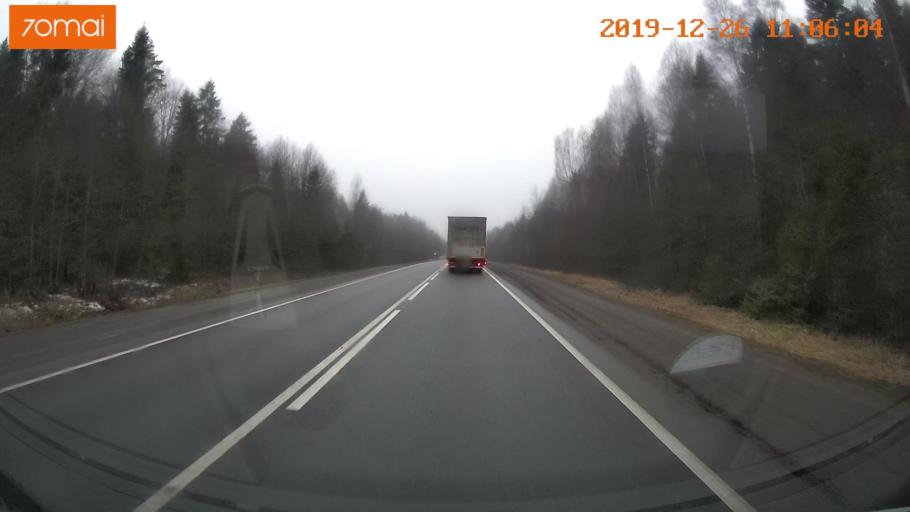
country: RU
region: Vologda
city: Molochnoye
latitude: 59.1436
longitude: 39.3289
